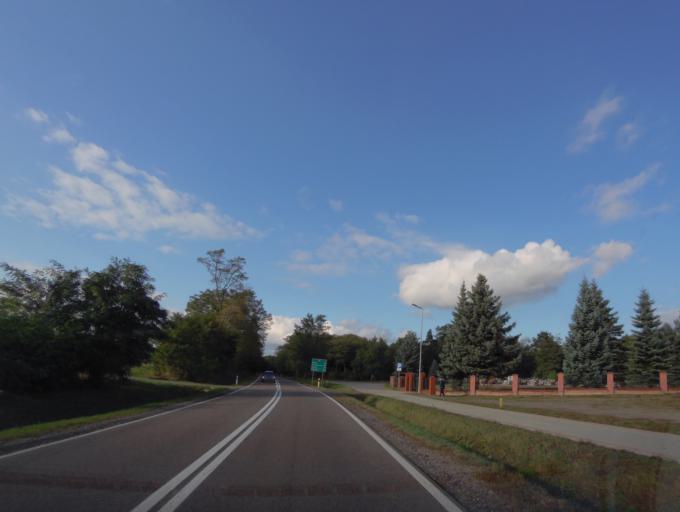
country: PL
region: Subcarpathian Voivodeship
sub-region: Powiat nizanski
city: Krzeszow
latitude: 50.3723
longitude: 22.3140
